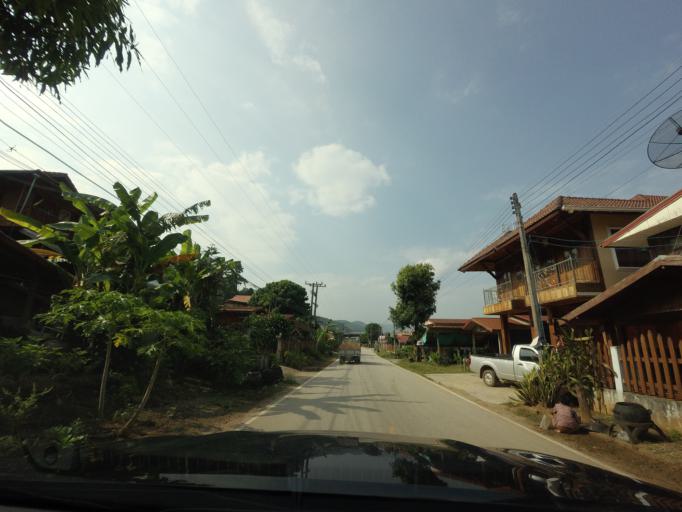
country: TH
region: Loei
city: Chiang Khan
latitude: 17.8452
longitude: 101.5696
